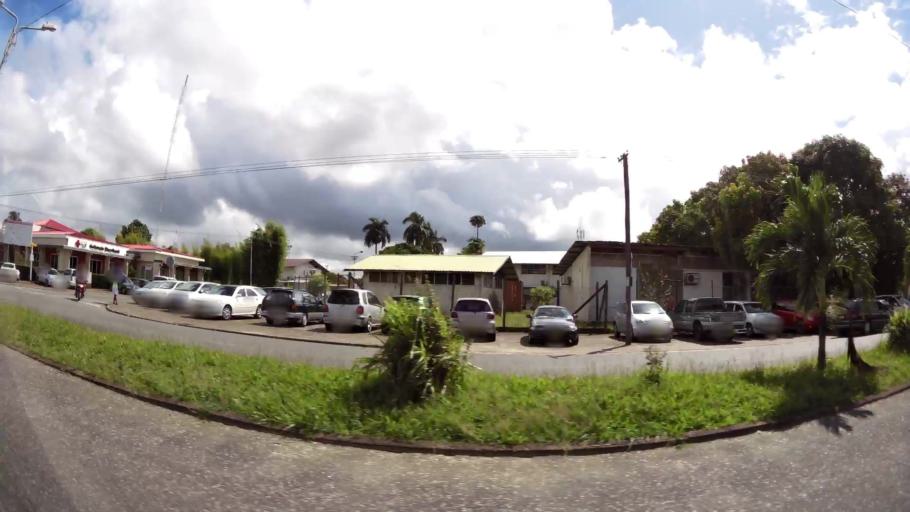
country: SR
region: Paramaribo
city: Paramaribo
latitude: 5.8285
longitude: -55.1787
